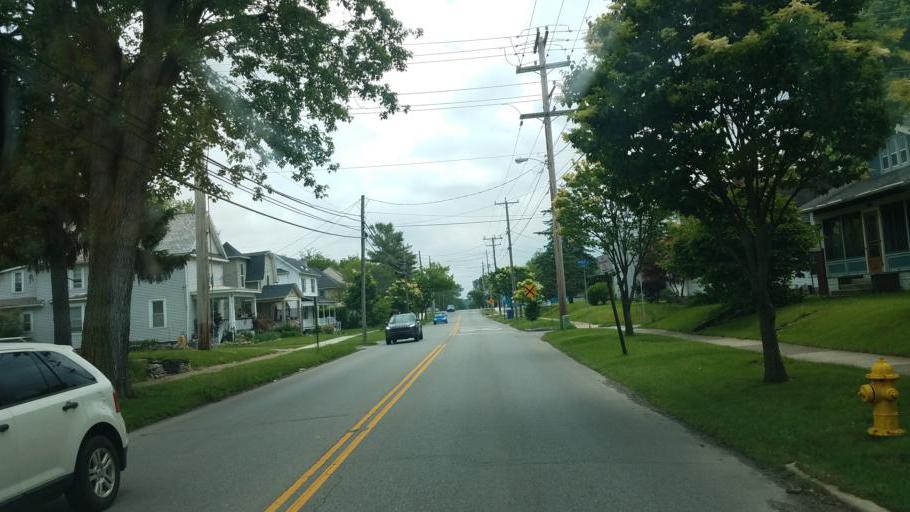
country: US
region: Ohio
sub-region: Delaware County
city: Delaware
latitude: 40.2996
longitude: -83.0845
